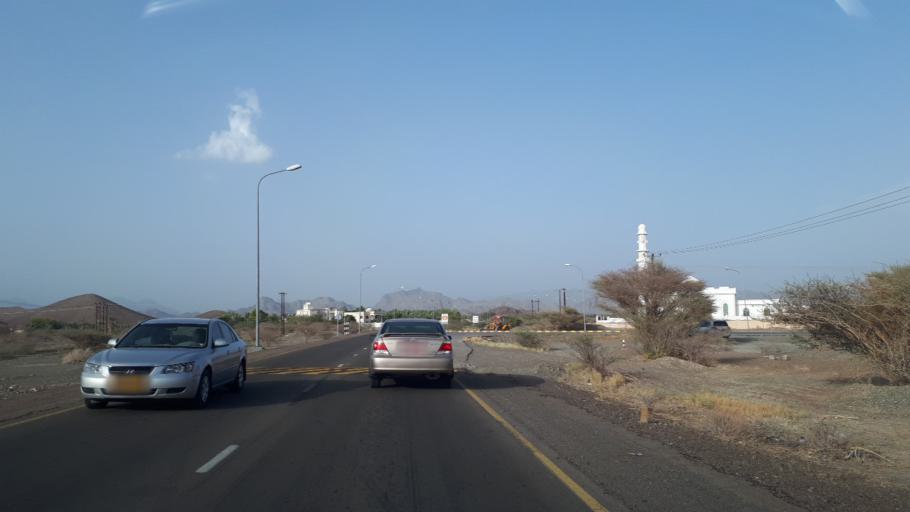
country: OM
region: Az Zahirah
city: Yanqul
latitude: 23.4303
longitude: 56.7641
